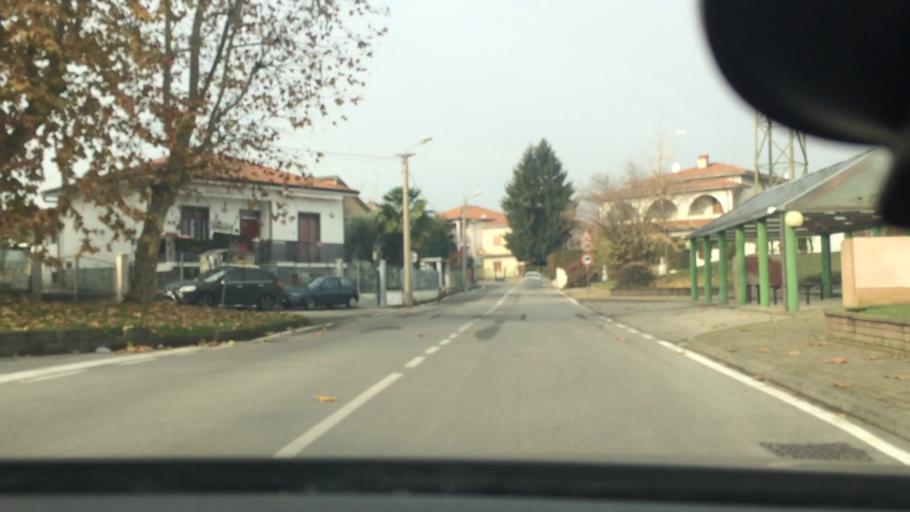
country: IT
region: Lombardy
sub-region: Provincia di Monza e Brianza
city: Villaggio del Sole
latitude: 45.6227
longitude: 9.1066
